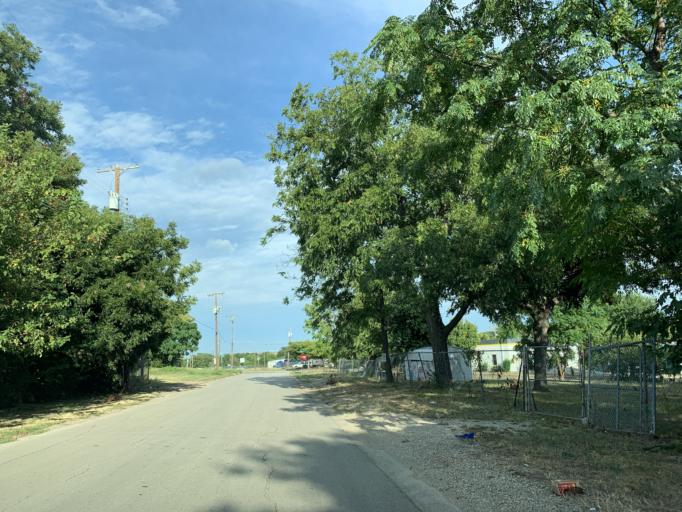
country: US
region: Texas
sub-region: Dallas County
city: Dallas
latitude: 32.7442
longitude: -96.8109
